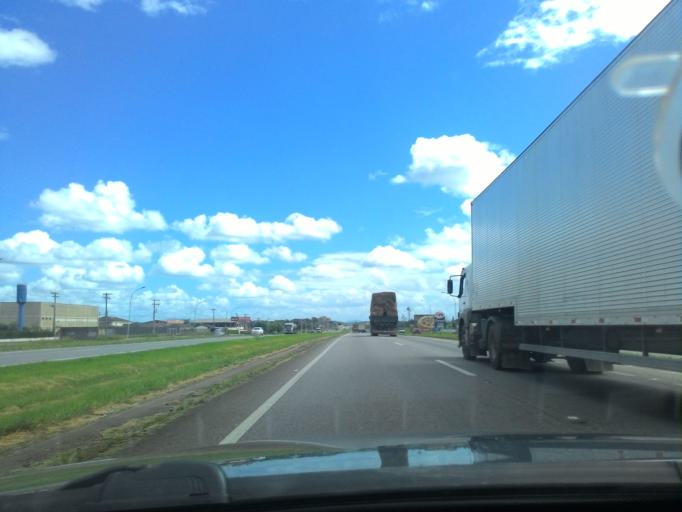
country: BR
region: Sao Paulo
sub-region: Registro
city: Registro
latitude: -24.5149
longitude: -47.8515
